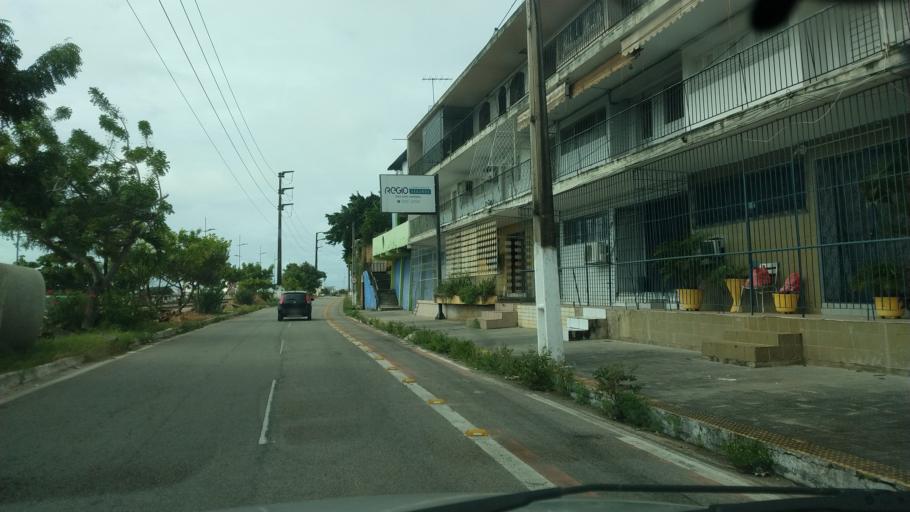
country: BR
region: Rio Grande do Norte
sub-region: Natal
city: Natal
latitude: -5.7843
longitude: -35.2107
